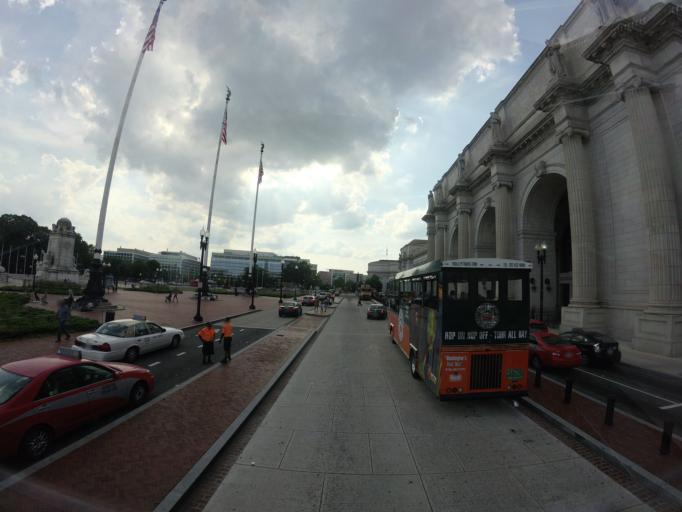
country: US
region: Washington, D.C.
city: Washington, D.C.
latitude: 38.8968
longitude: -77.0059
